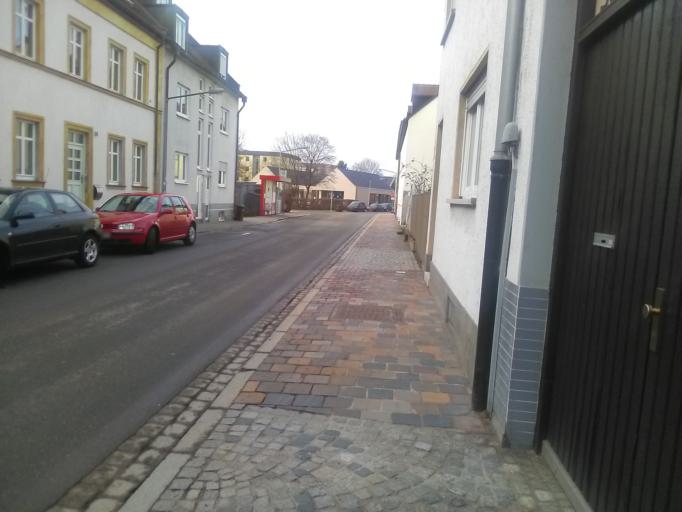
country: DE
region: Bavaria
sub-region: Upper Franconia
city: Bamberg
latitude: 49.8882
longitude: 10.9096
